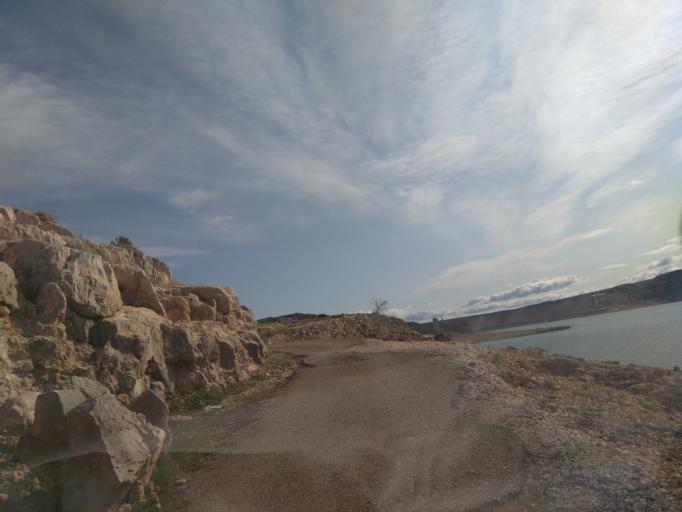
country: ES
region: Valencia
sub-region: Provincia de Valencia
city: Sumacarcer
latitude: 39.1534
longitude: -0.6568
